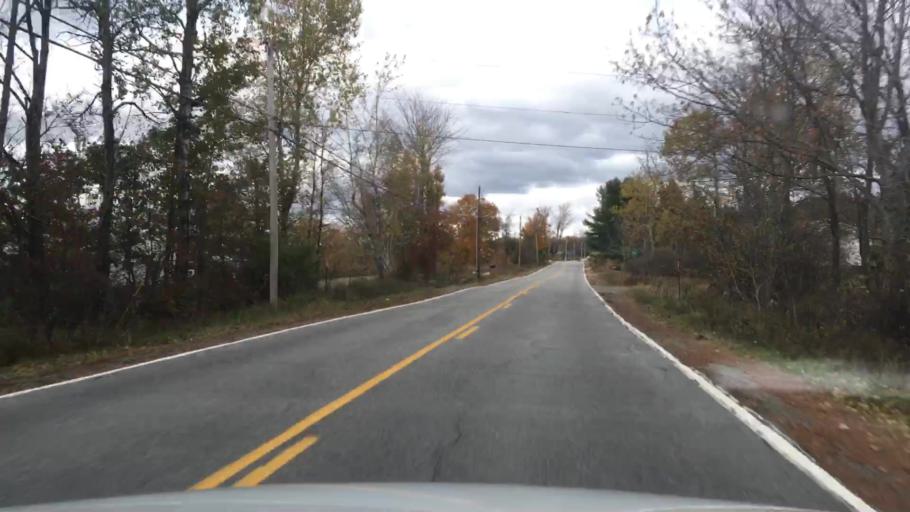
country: US
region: Maine
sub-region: Androscoggin County
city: Sabattus
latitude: 44.1592
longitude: -70.0791
